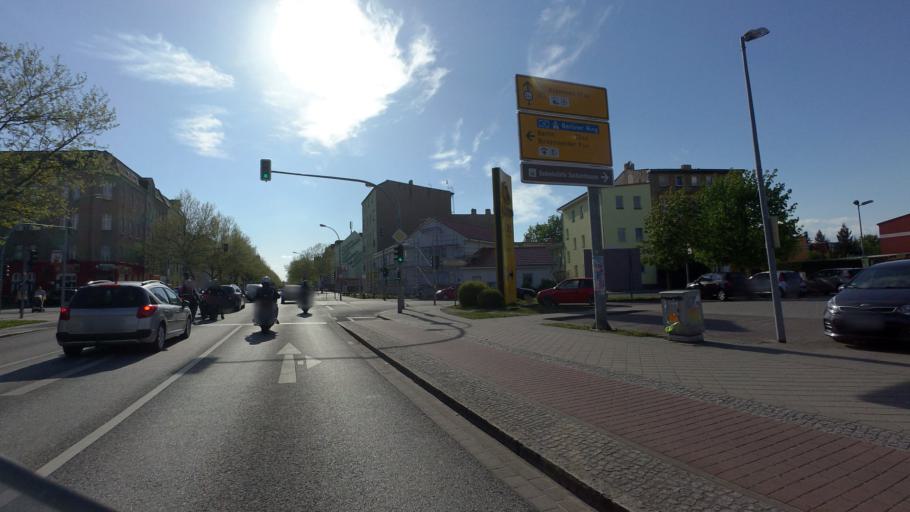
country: DE
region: Brandenburg
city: Oranienburg
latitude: 52.7588
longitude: 13.2555
